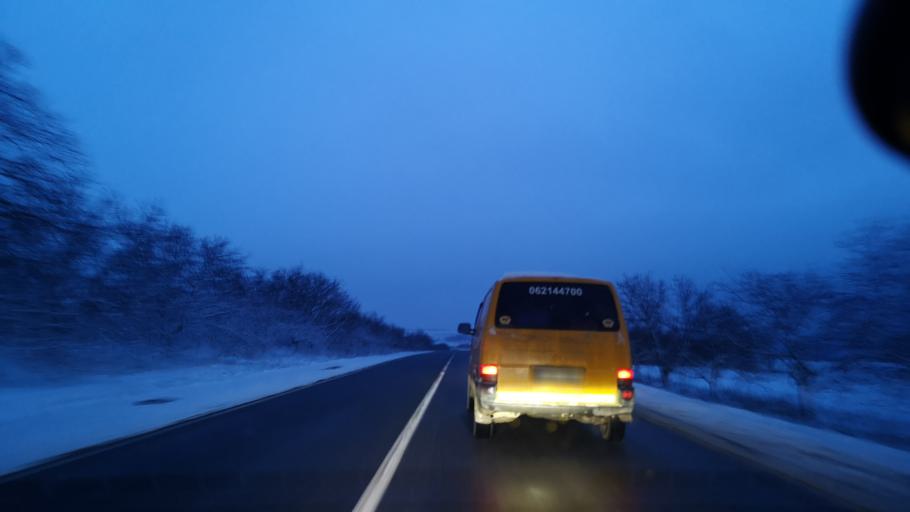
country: MD
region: Rezina
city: Saharna
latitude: 47.6163
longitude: 28.8321
